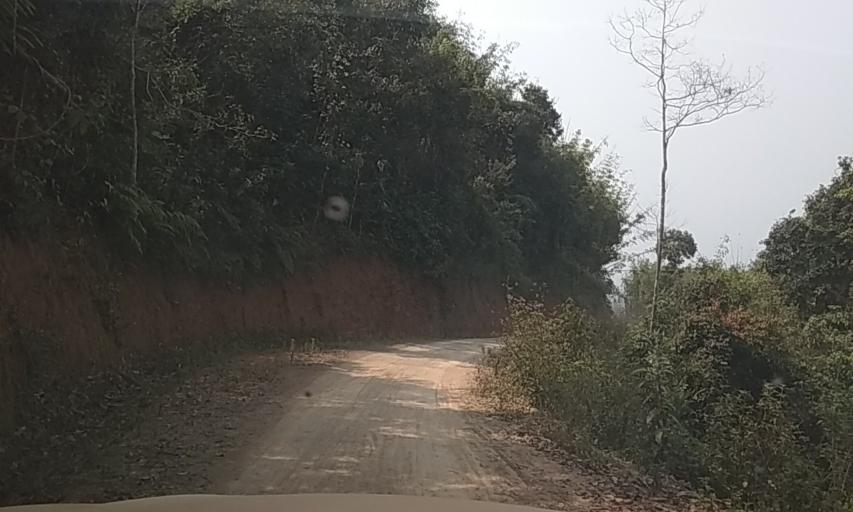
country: LA
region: Phongsali
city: Phongsali
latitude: 21.4642
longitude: 102.4189
